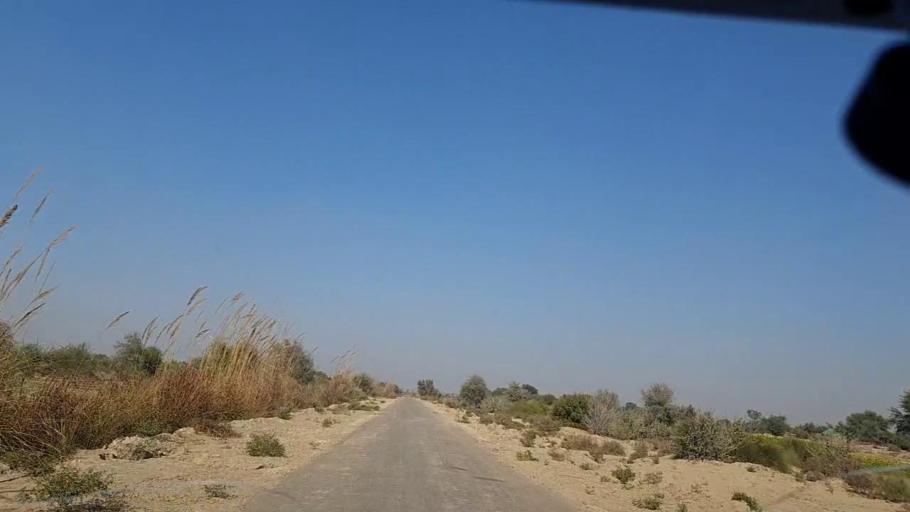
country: PK
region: Sindh
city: Khanpur
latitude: 27.5678
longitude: 69.3797
